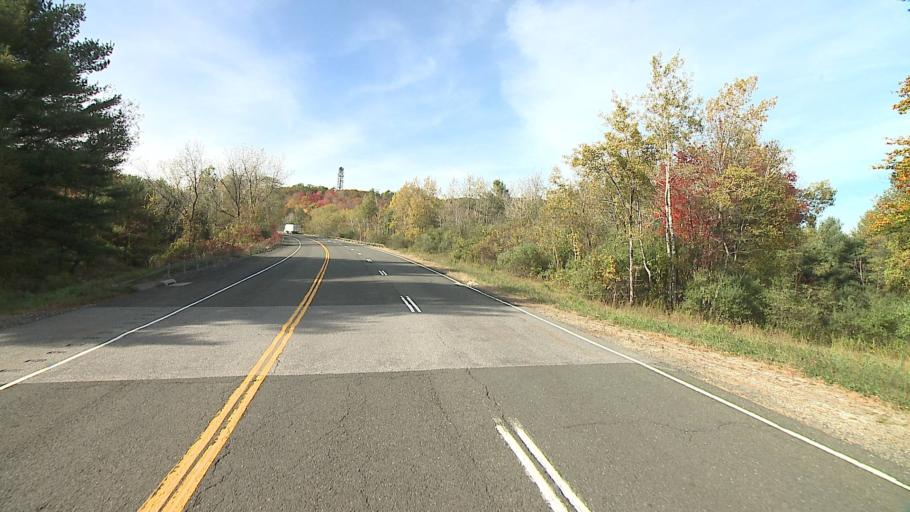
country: US
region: Connecticut
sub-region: Litchfield County
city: Winsted
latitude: 41.9366
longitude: -73.0912
